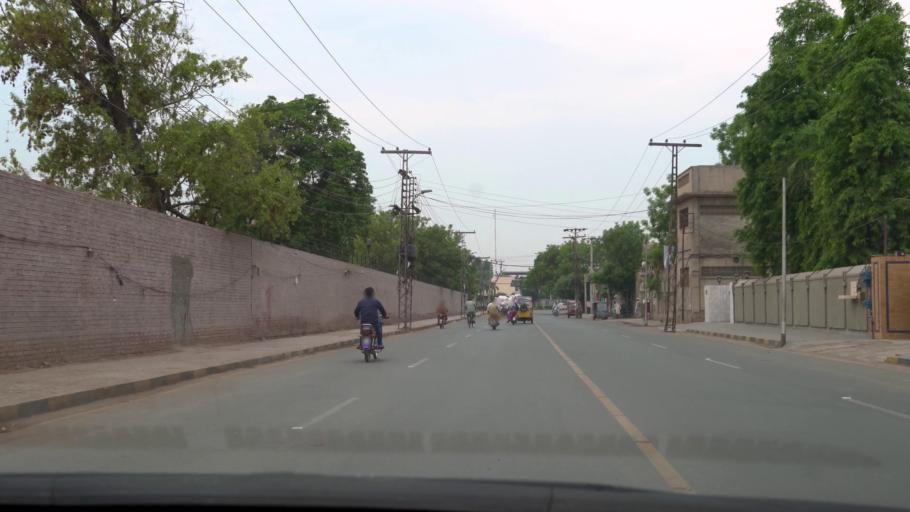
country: PK
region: Punjab
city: Faisalabad
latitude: 31.4305
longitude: 73.0831
